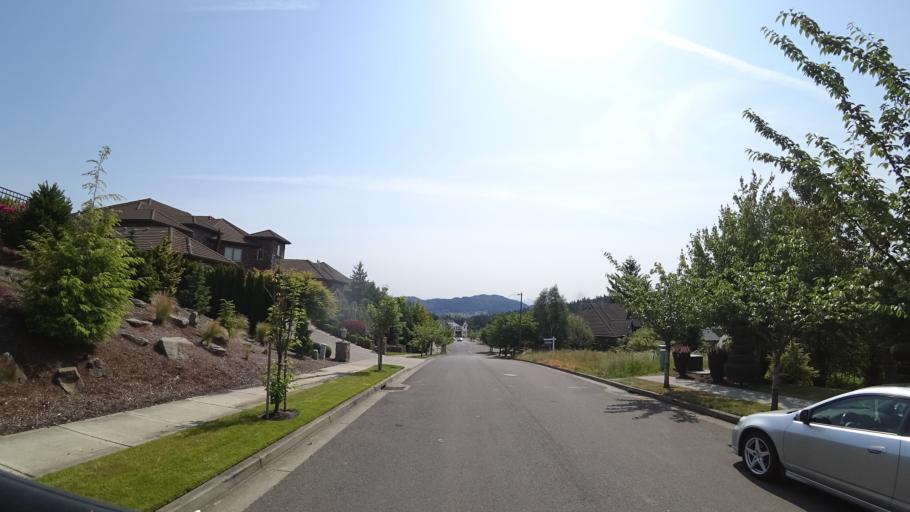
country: US
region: Oregon
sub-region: Clackamas County
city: Happy Valley
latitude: 45.4585
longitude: -122.5126
